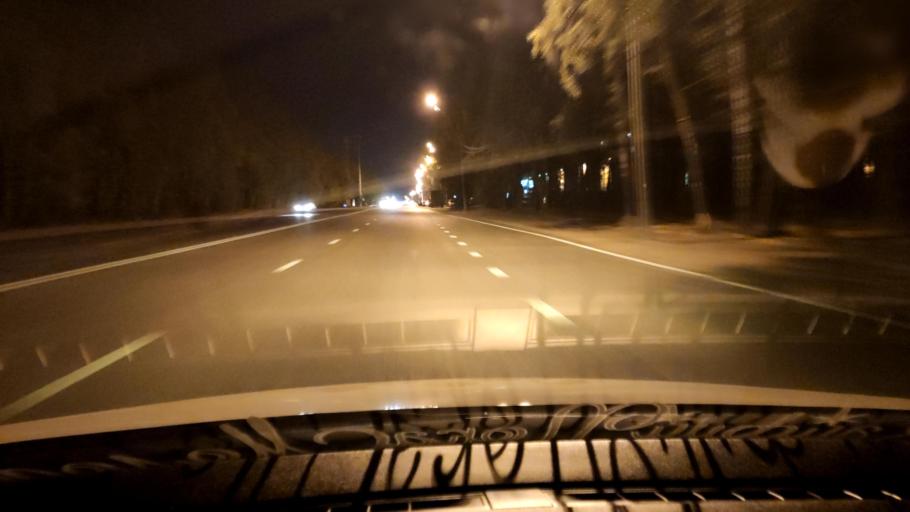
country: RU
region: Voronezj
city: Pridonskoy
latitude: 51.6891
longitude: 39.1046
